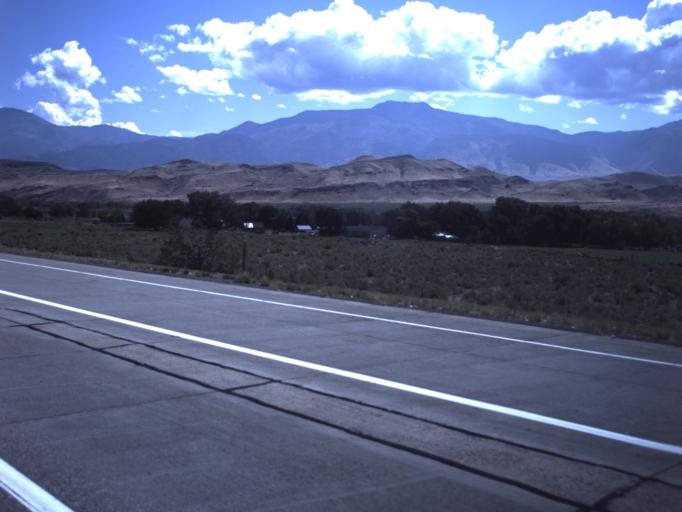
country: US
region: Utah
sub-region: Sevier County
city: Monroe
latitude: 38.6005
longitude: -112.2506
